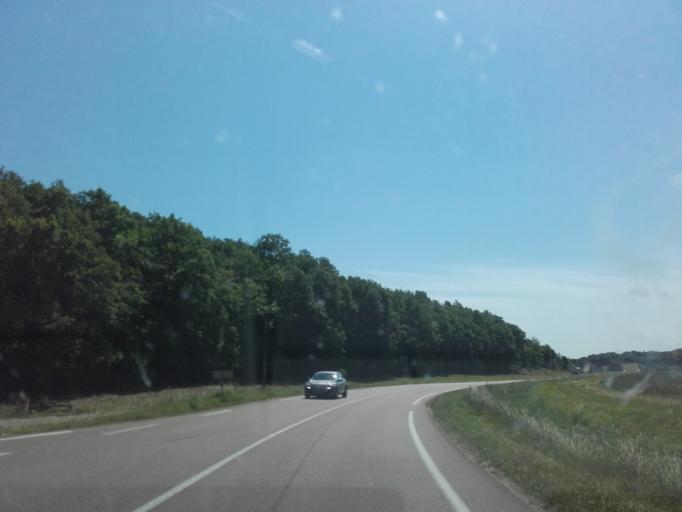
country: FR
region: Bourgogne
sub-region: Departement de l'Yonne
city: Chablis
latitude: 47.7451
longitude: 3.8294
